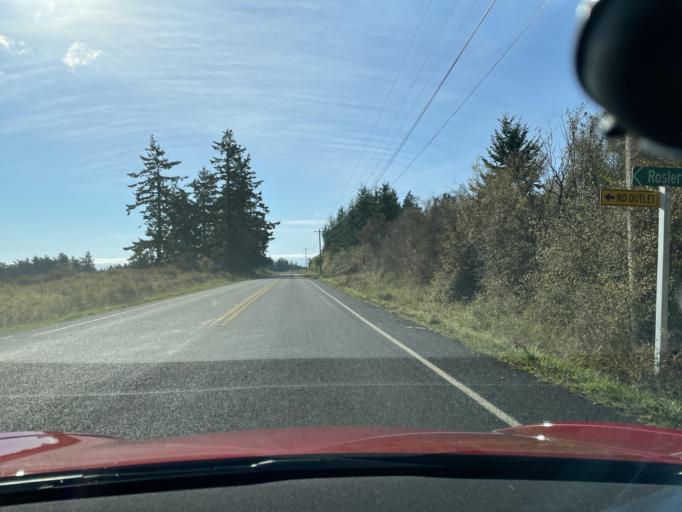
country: US
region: Washington
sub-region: San Juan County
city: Friday Harbor
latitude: 48.4794
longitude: -123.0322
